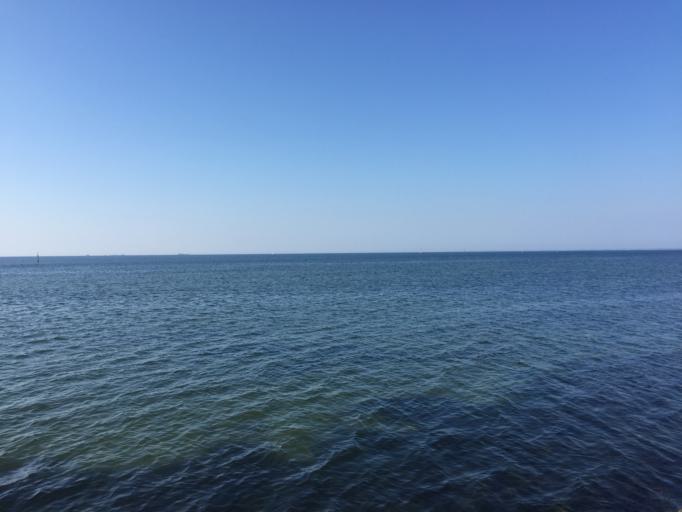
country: DK
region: Zealand
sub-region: Lolland Kommune
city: Nakskov
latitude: 54.8773
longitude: 11.0239
